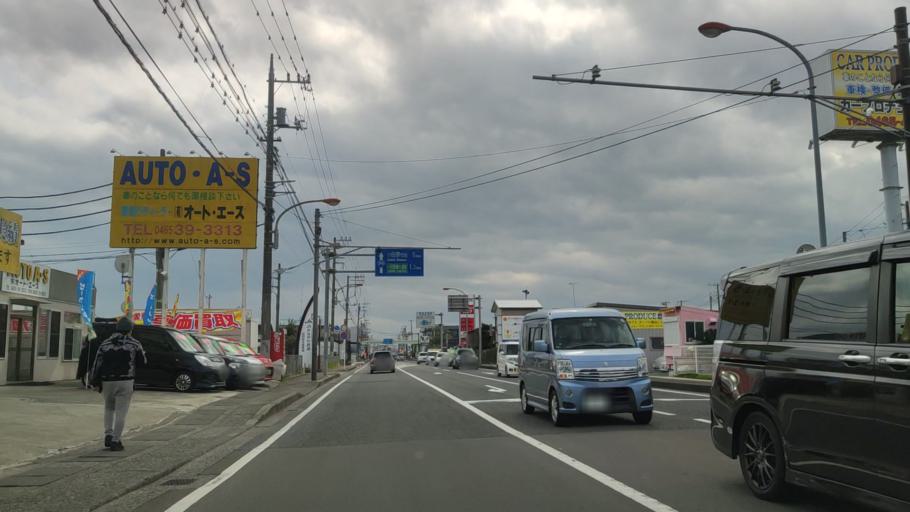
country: JP
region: Kanagawa
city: Odawara
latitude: 35.2978
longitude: 139.1671
